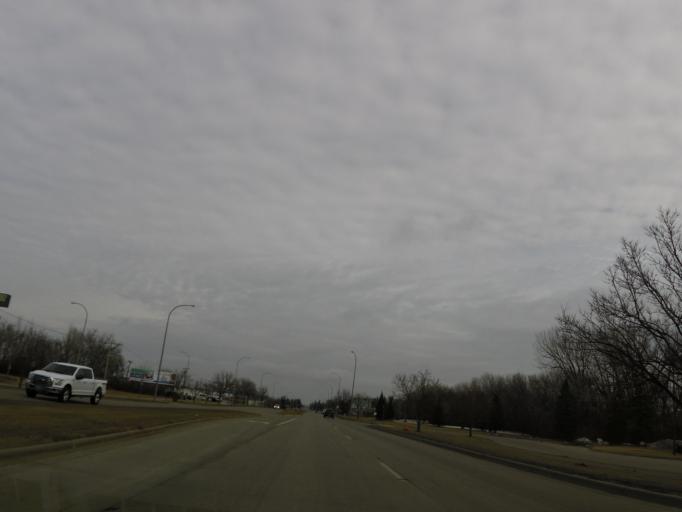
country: US
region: North Dakota
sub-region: Grand Forks County
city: Grand Forks
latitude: 47.9329
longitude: -97.0780
